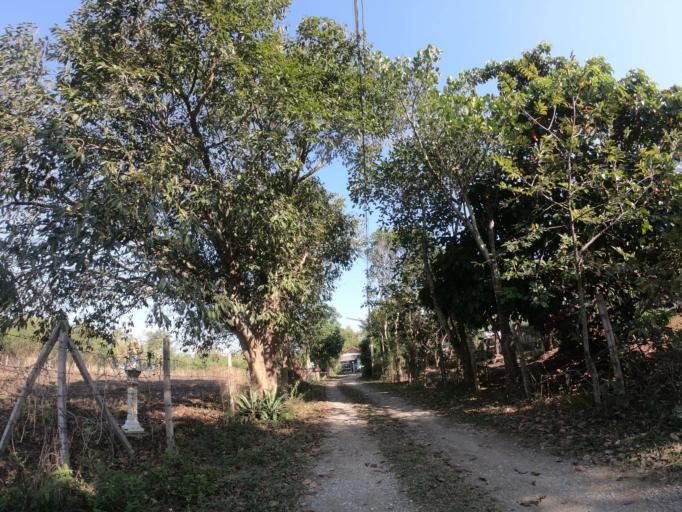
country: TH
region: Chiang Mai
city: Chiang Mai
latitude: 18.7548
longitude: 98.9788
